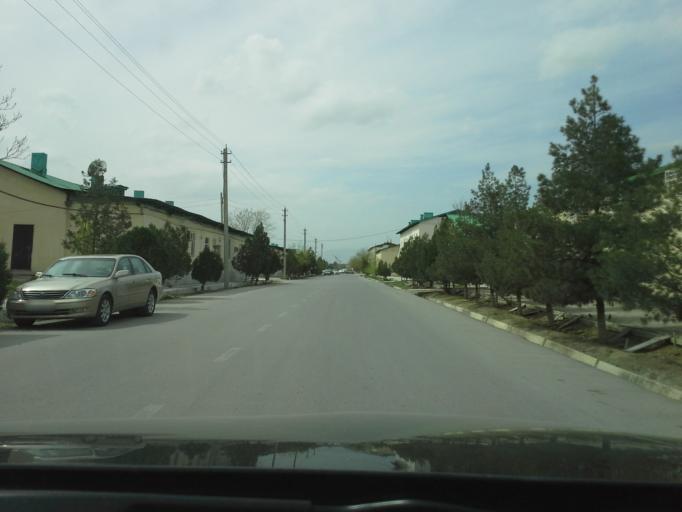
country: TM
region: Ahal
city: Abadan
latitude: 38.0572
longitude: 58.1550
